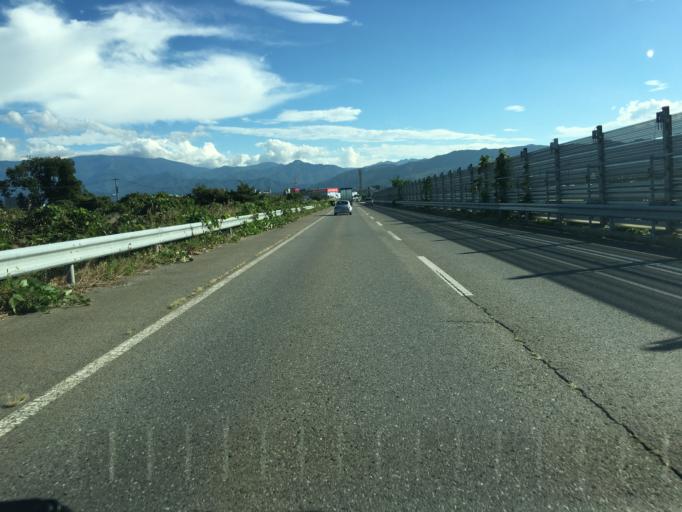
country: JP
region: Yamagata
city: Yonezawa
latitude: 37.9332
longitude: 140.1102
